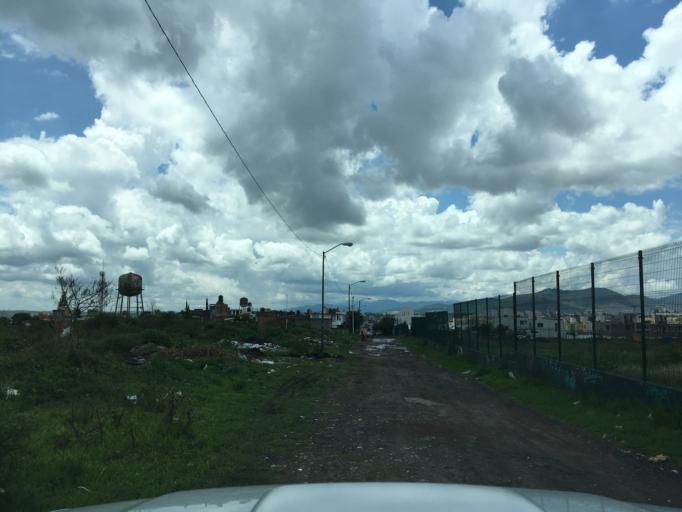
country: MX
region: Michoacan
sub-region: Tarimbaro
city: Real Hacienda (Metropolis)
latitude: 19.7299
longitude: -101.2104
